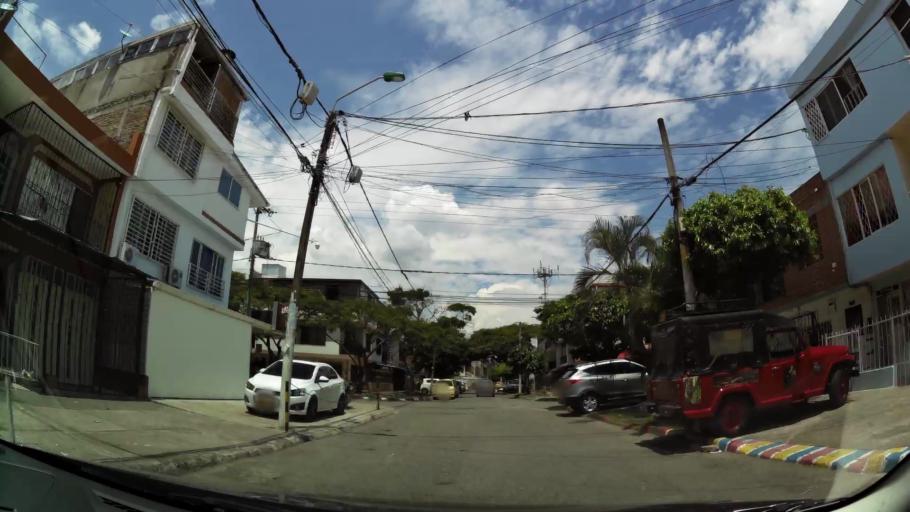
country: CO
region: Valle del Cauca
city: Cali
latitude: 3.4425
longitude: -76.5050
